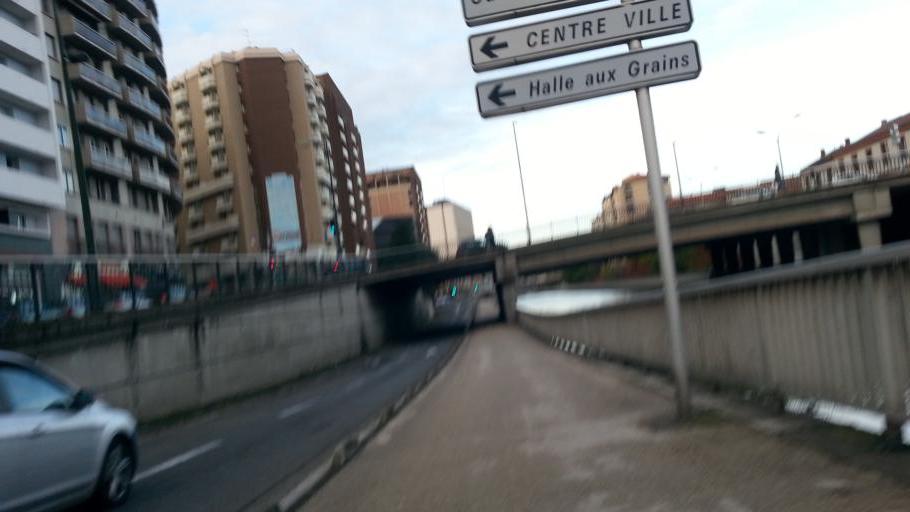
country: FR
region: Midi-Pyrenees
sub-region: Departement de la Haute-Garonne
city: Toulouse
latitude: 43.5980
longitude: 1.4561
